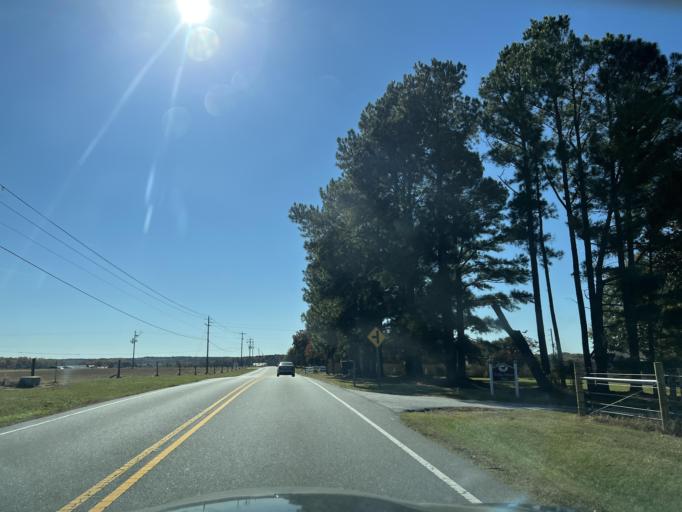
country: US
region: North Carolina
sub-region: Wake County
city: West Raleigh
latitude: 35.7322
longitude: -78.6826
